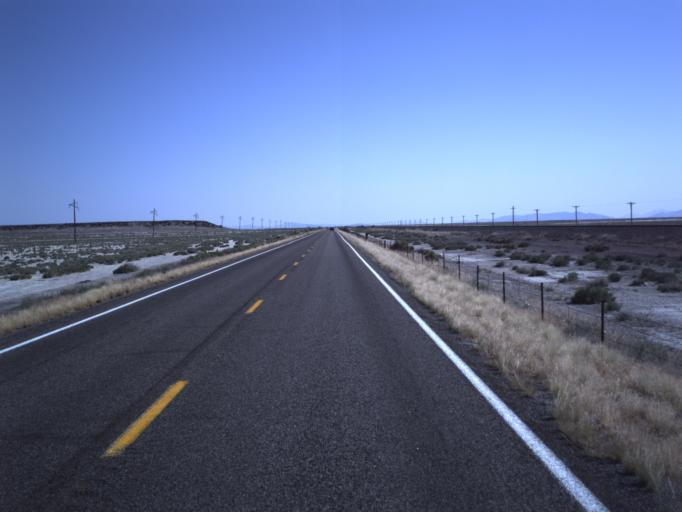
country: US
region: Utah
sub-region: Millard County
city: Delta
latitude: 39.1720
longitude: -112.7055
